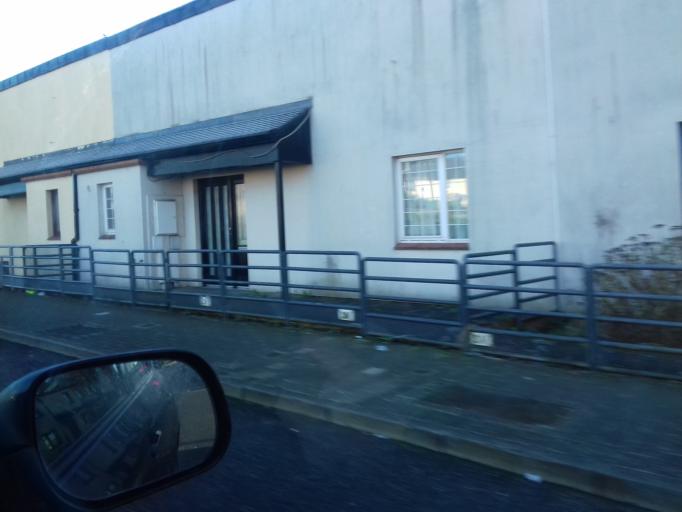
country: IE
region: Leinster
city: Ballymun
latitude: 53.3998
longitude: -6.2756
